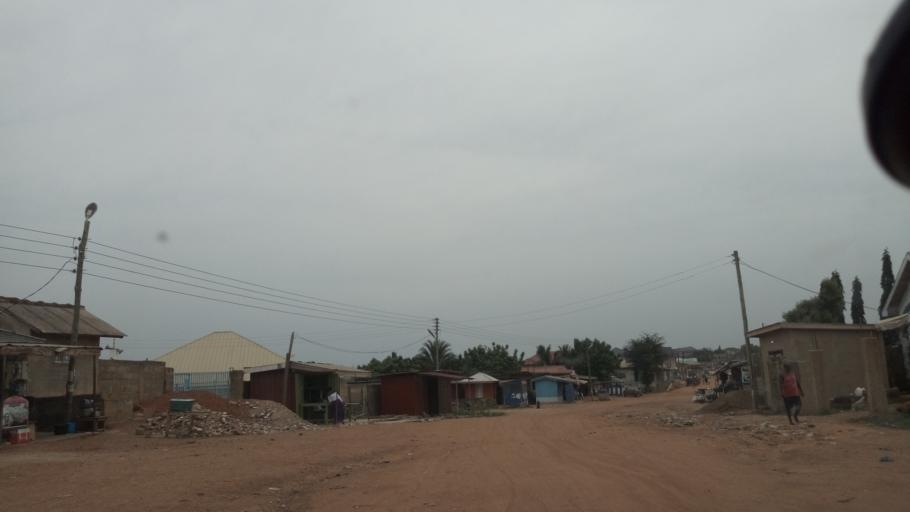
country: GH
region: Greater Accra
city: Medina Estates
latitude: 5.7118
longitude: -0.1287
